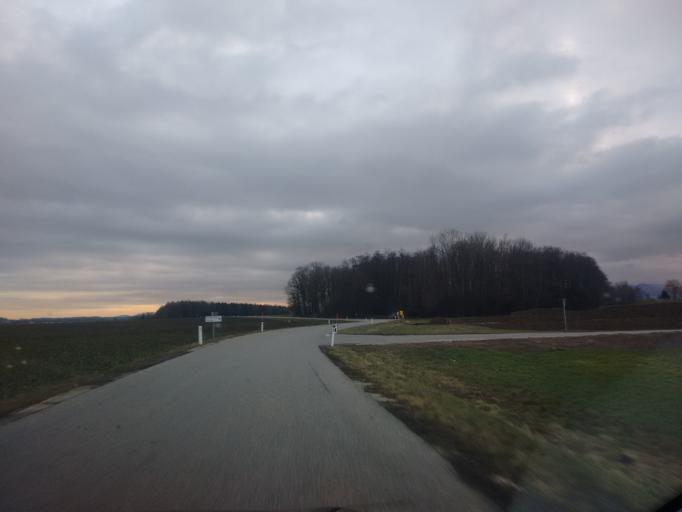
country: AT
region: Upper Austria
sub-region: Politischer Bezirk Steyr-Land
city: Pfarrkirchen bei Bad Hall
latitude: 48.0429
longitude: 14.1872
